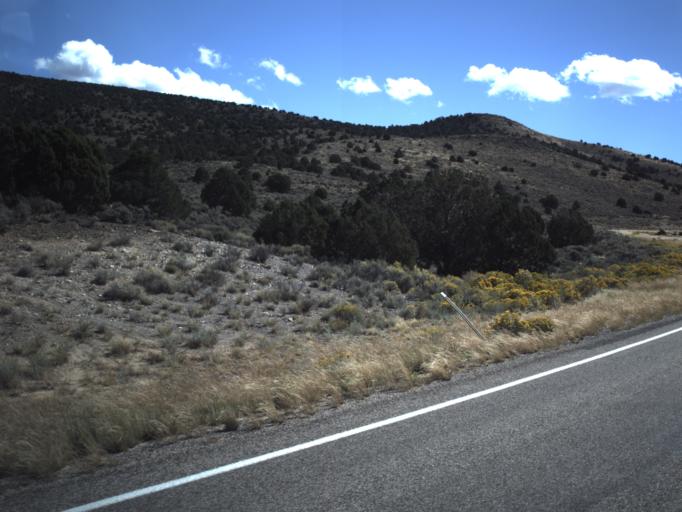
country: US
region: Utah
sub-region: Beaver County
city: Milford
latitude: 38.1132
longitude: -112.9514
